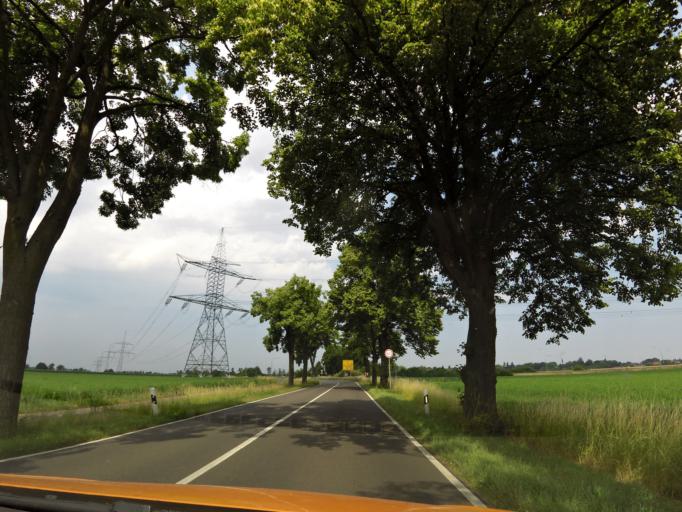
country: DE
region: Brandenburg
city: Nauen
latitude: 52.5917
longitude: 12.8751
